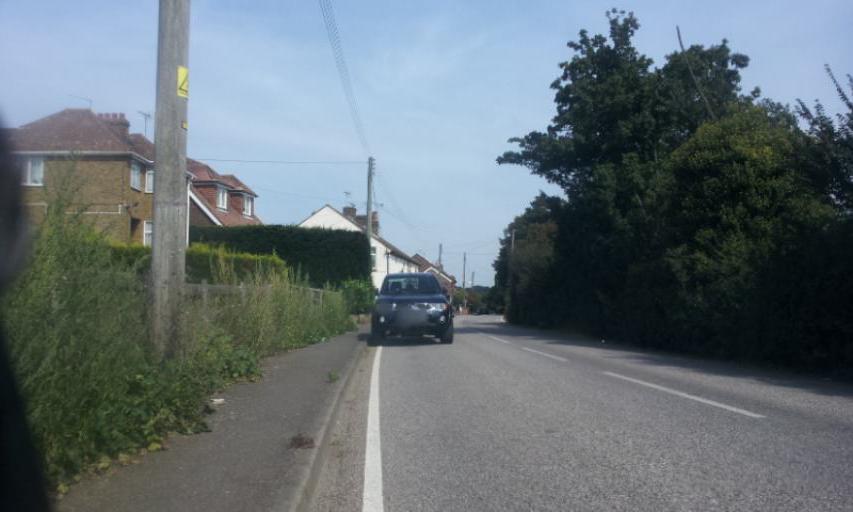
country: GB
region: England
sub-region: Kent
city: Newington
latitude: 51.3428
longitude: 0.6898
